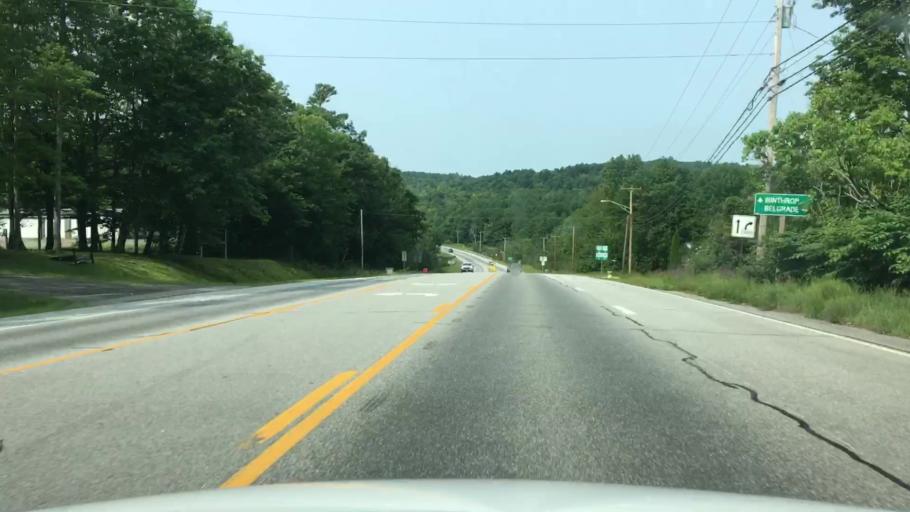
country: US
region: Maine
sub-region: Kennebec County
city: Winthrop
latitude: 44.3198
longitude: -69.9264
